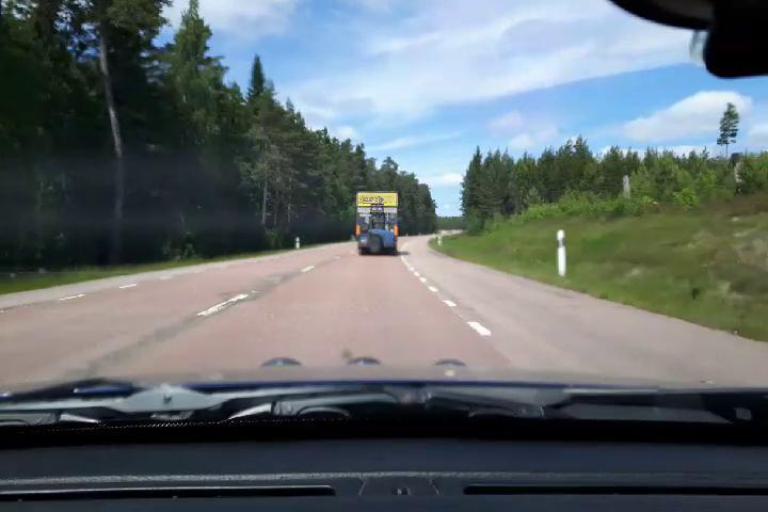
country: SE
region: Uppsala
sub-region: Osthammars Kommun
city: Bjorklinge
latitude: 60.1245
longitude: 17.5092
